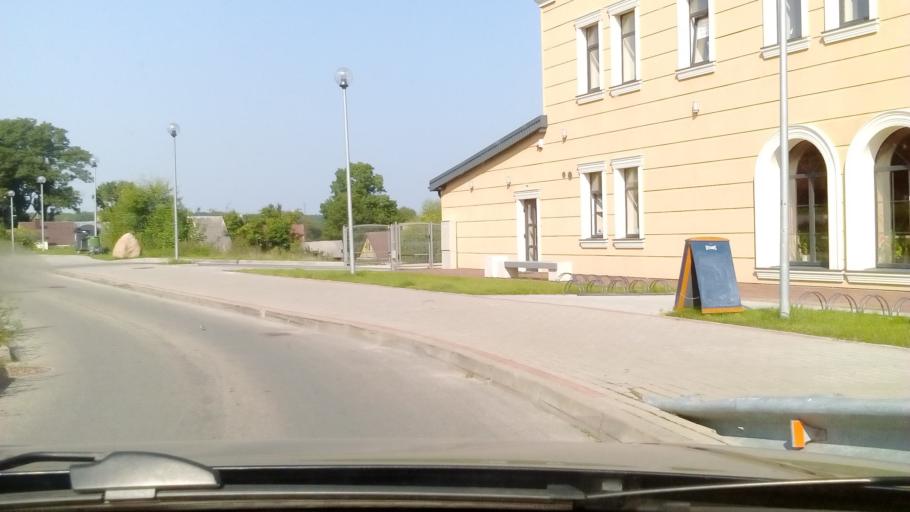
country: LT
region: Alytaus apskritis
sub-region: Alytus
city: Alytus
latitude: 54.4006
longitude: 24.0527
